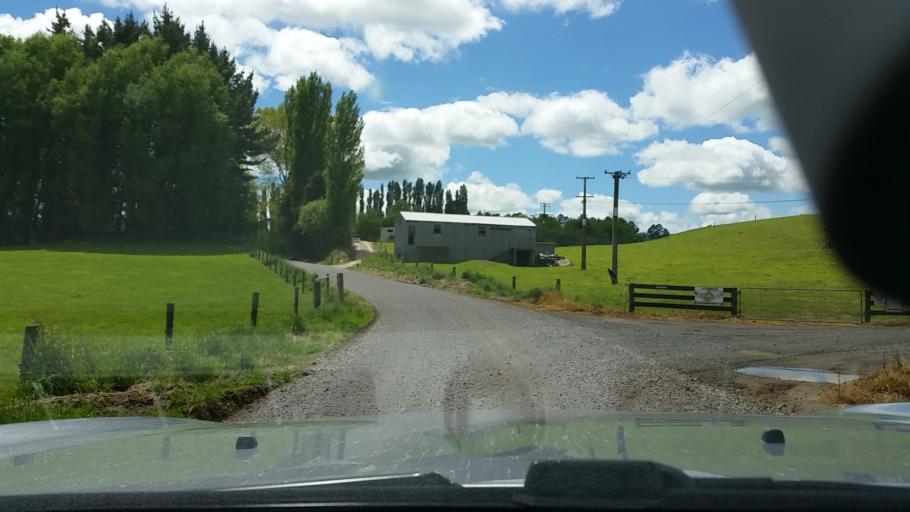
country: NZ
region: Waikato
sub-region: South Waikato District
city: Tokoroa
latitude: -38.3633
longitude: 176.0657
